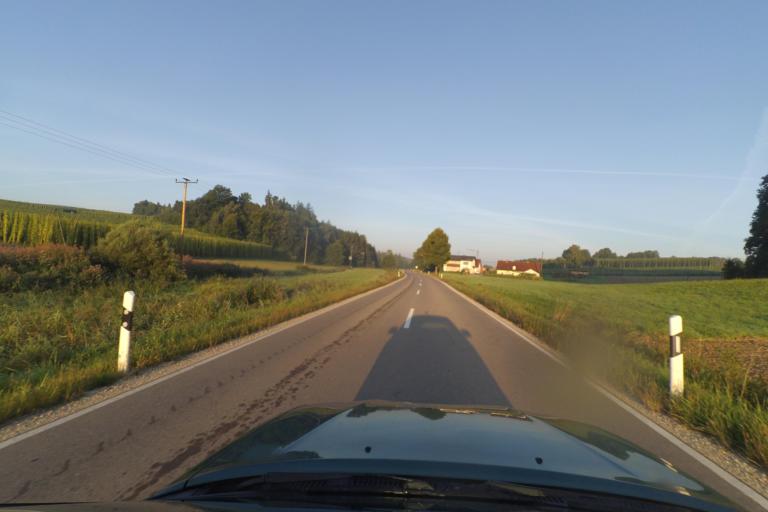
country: DE
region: Bavaria
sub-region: Lower Bavaria
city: Aiglsbach
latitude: 48.6711
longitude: 11.6952
